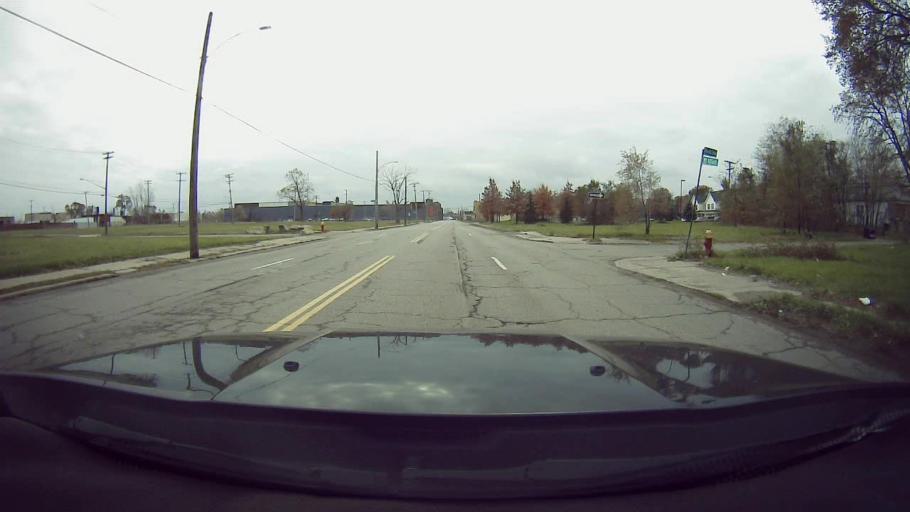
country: US
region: Michigan
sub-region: Wayne County
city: Hamtramck
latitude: 42.3954
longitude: -83.0375
